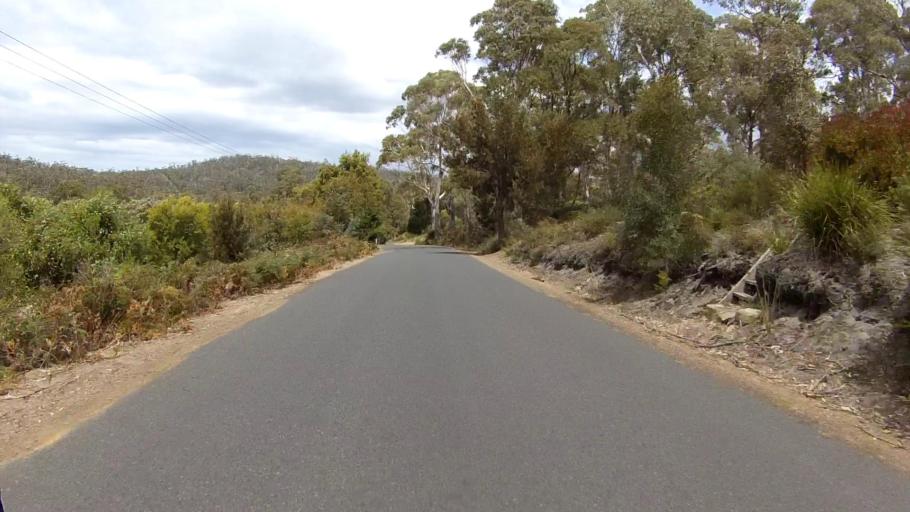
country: AU
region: Tasmania
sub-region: Sorell
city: Sorell
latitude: -42.5882
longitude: 147.9148
